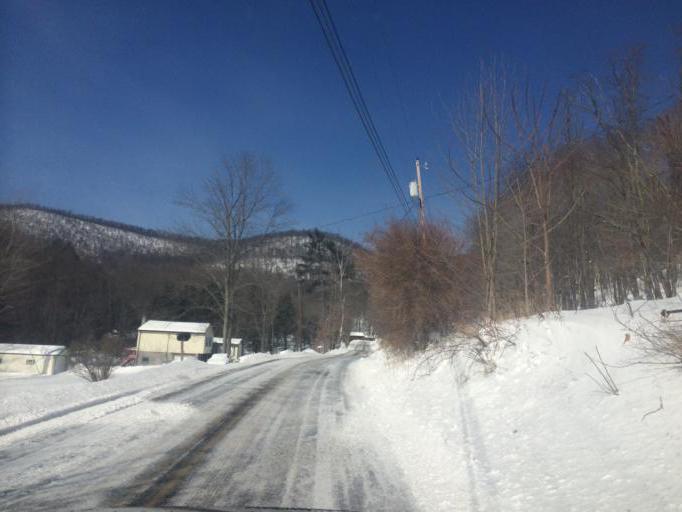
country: US
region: Pennsylvania
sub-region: Centre County
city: Stormstown
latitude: 40.8622
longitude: -78.0276
